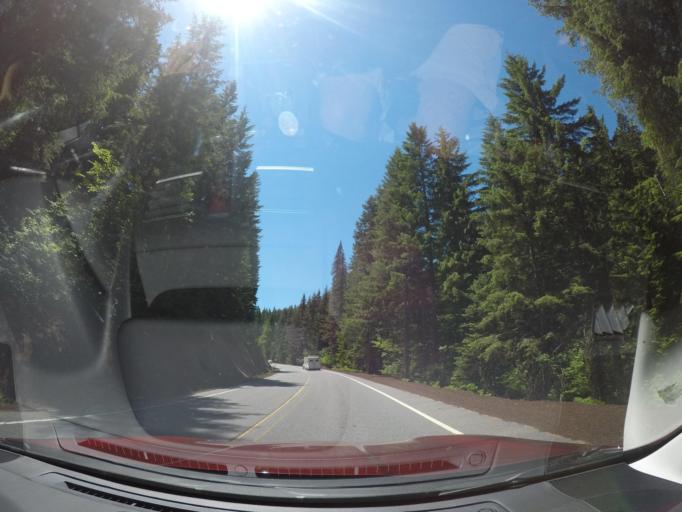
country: US
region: Oregon
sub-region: Deschutes County
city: Sisters
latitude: 44.5443
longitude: -121.9956
